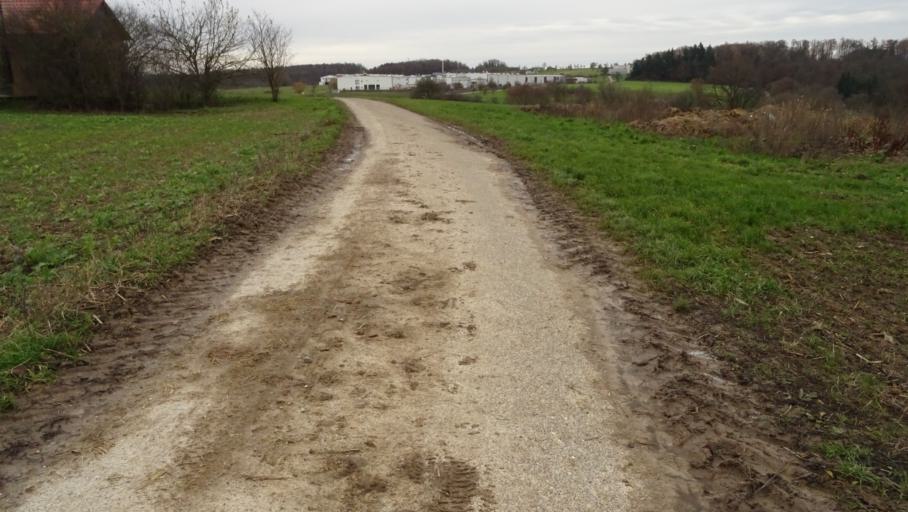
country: DE
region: Baden-Wuerttemberg
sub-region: Karlsruhe Region
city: Binau
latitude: 49.3419
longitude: 9.0482
